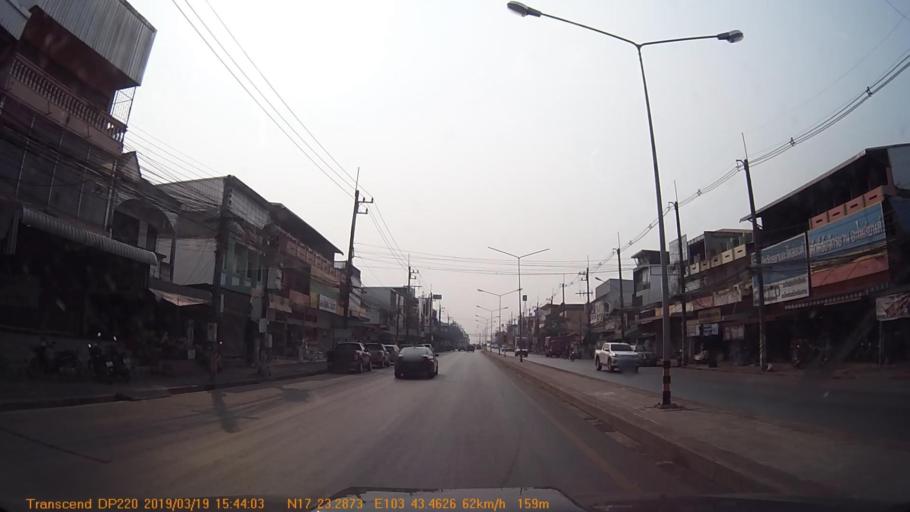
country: TH
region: Sakon Nakhon
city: Phang Khon
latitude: 17.3882
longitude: 103.7242
